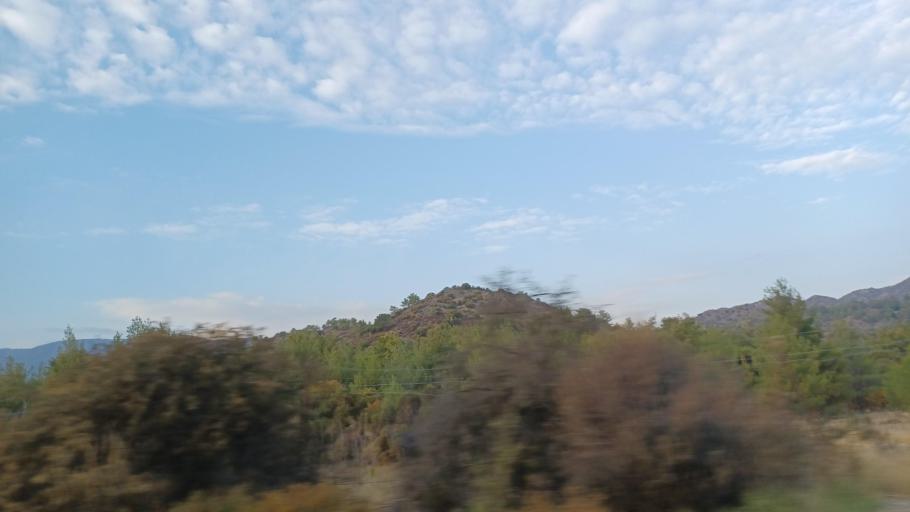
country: CY
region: Limassol
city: Pelendri
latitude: 34.8585
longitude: 32.9276
